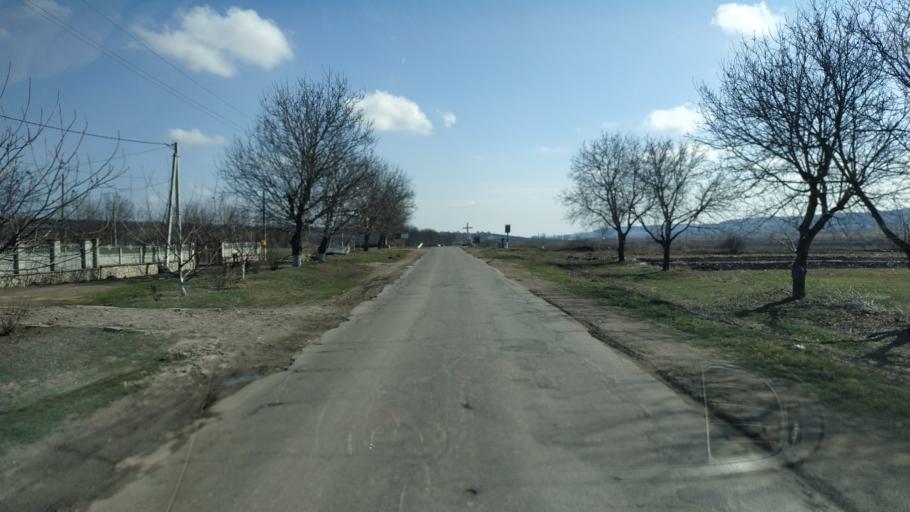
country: MD
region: Laloveni
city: Ialoveni
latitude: 46.9290
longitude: 28.6720
